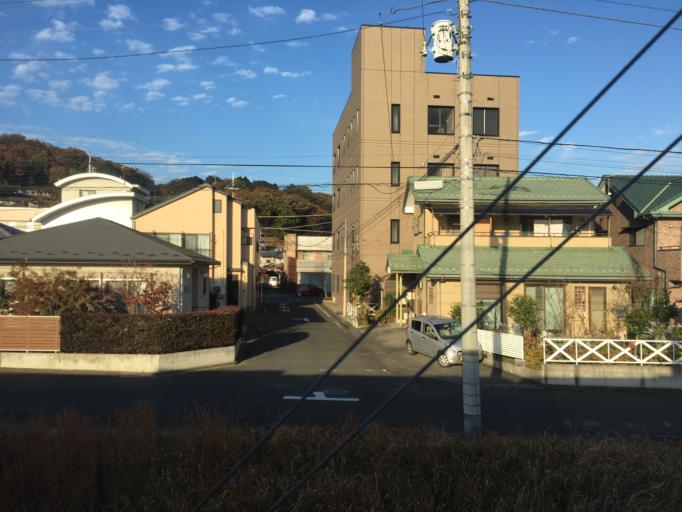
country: JP
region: Gunma
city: Kiryu
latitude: 36.4126
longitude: 139.3303
